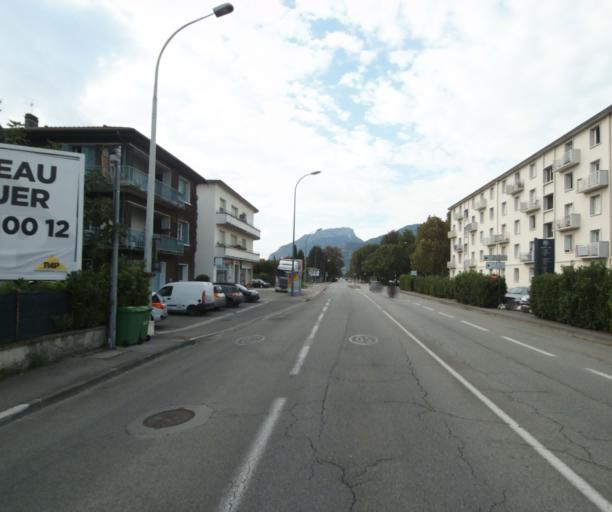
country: FR
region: Rhone-Alpes
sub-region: Departement de l'Isere
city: Eybens
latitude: 45.1665
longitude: 5.7419
